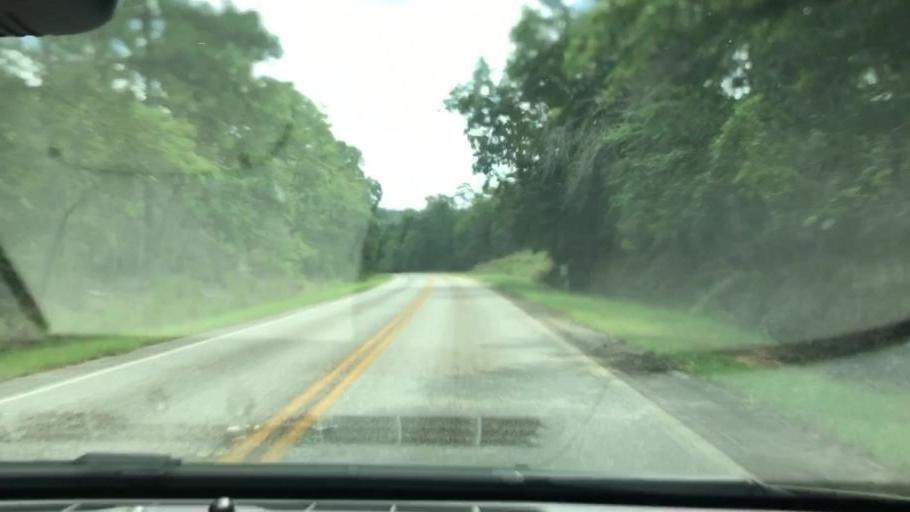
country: US
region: Georgia
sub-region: Stewart County
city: Lumpkin
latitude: 32.0588
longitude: -84.8178
